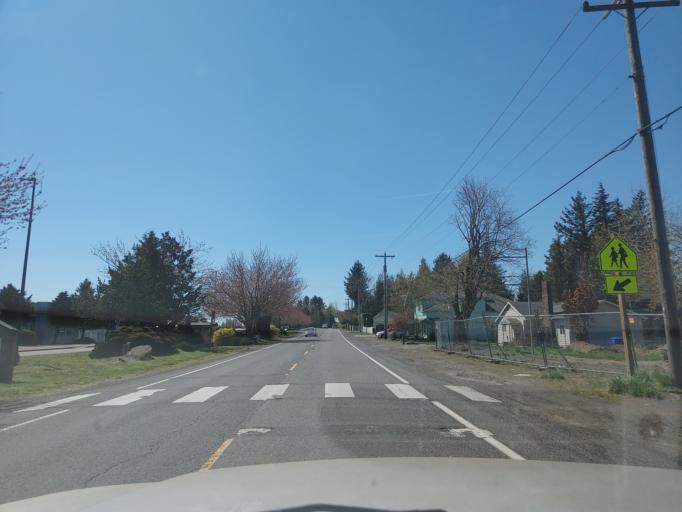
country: US
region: Washington
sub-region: Clark County
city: Washougal
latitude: 45.5310
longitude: -122.2943
